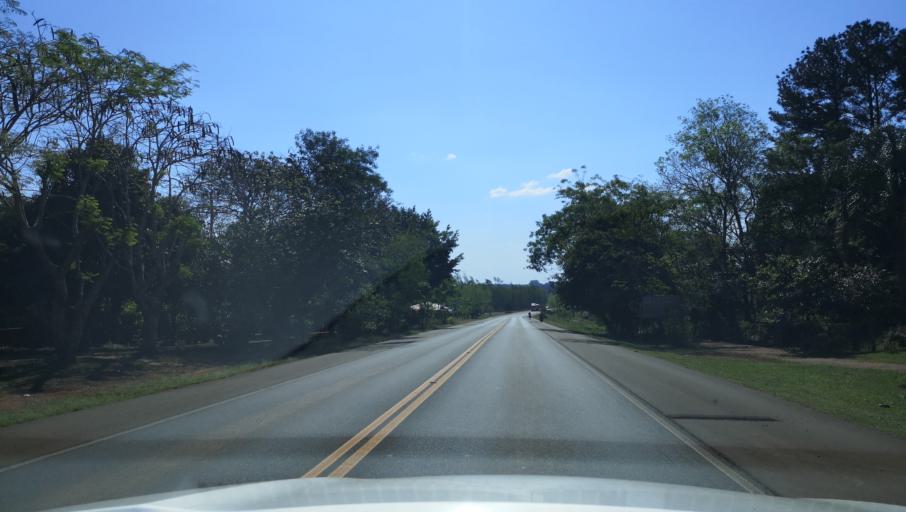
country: PY
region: Misiones
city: Santiago
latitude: -27.0441
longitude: -56.6555
